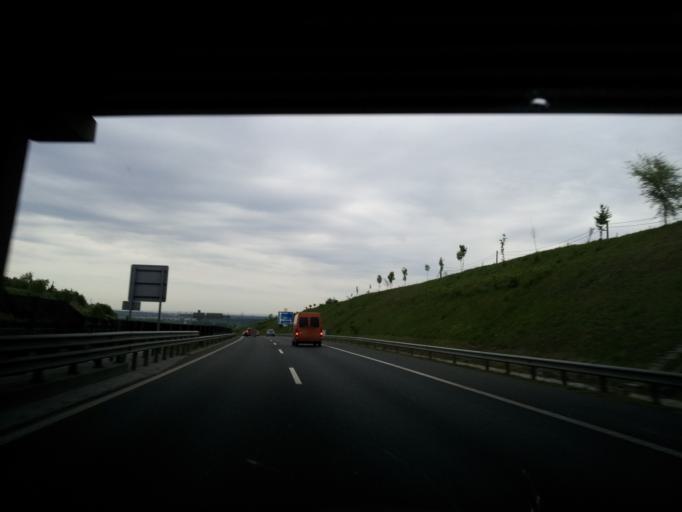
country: HU
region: Pest
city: Erd
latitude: 47.3626
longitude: 18.9176
